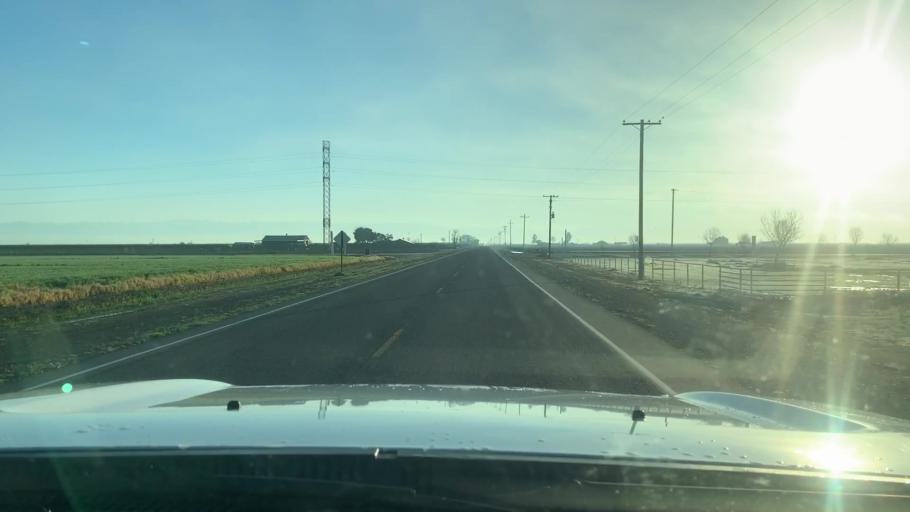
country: US
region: California
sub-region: Kings County
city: Home Garden
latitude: 36.2110
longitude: -119.5935
